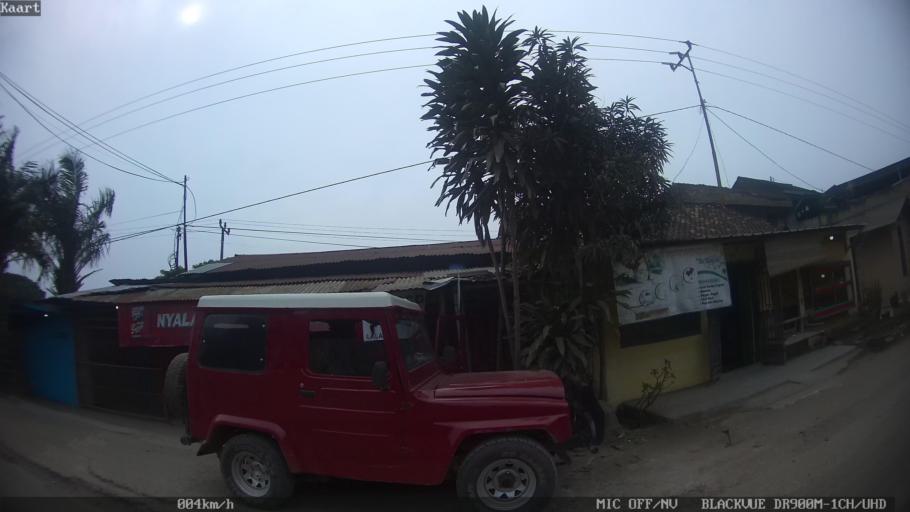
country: ID
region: Lampung
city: Panjang
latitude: -5.4261
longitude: 105.3295
